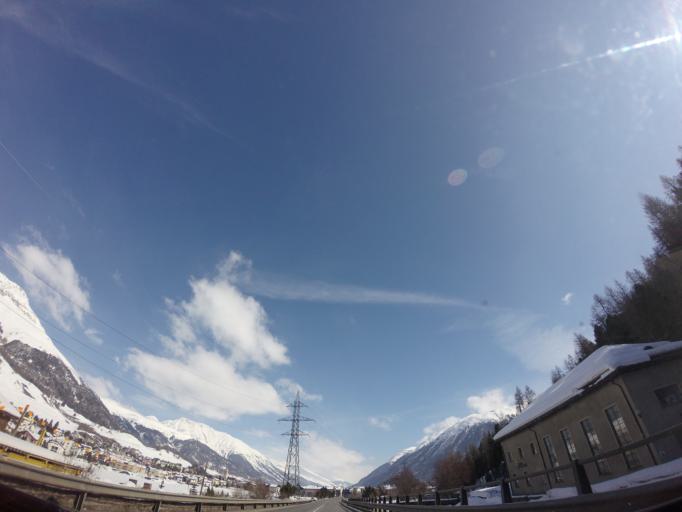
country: CH
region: Grisons
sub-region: Maloja District
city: Celerina
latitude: 46.5056
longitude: 9.8568
